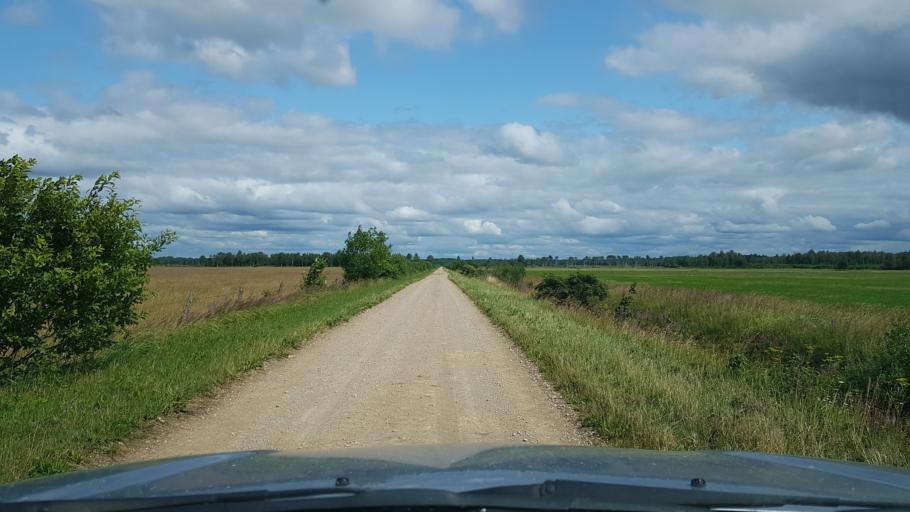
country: EE
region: Ida-Virumaa
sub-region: Sillamaee linn
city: Sillamae
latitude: 59.3703
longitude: 27.8960
